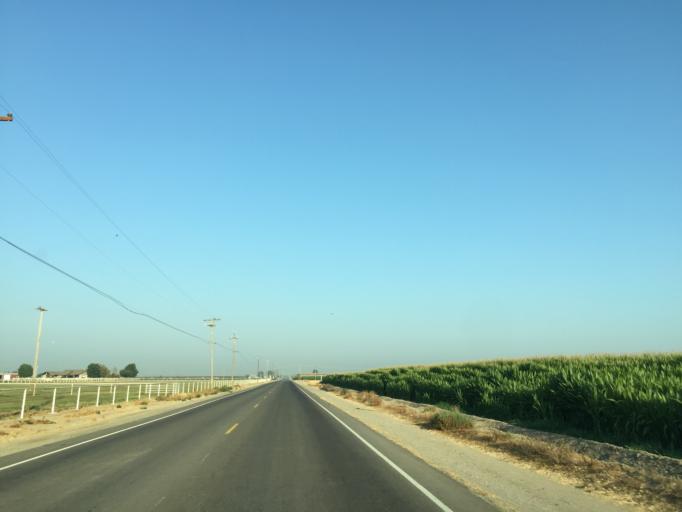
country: US
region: California
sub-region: Tulare County
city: London
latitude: 36.4584
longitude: -119.3809
